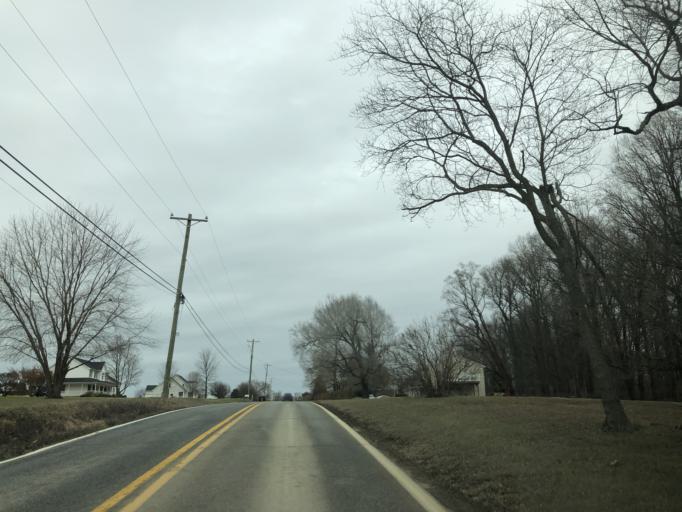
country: US
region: Delaware
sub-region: New Castle County
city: Middletown
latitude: 39.4853
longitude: -75.6960
